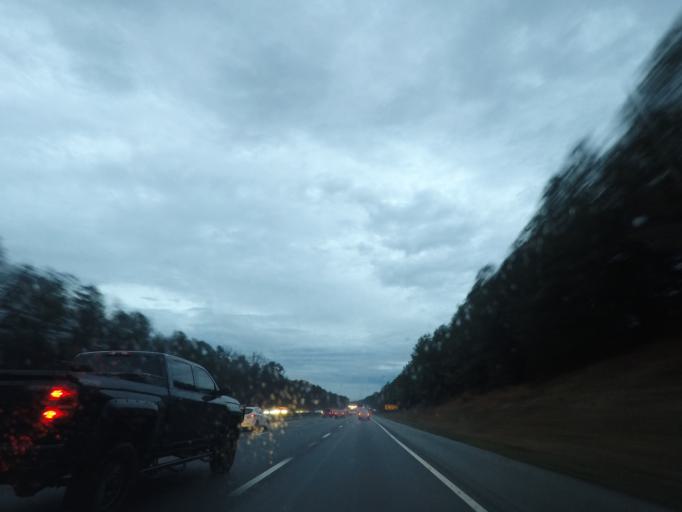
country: US
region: North Carolina
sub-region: Orange County
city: Chapel Hill
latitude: 35.9335
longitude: -78.9890
